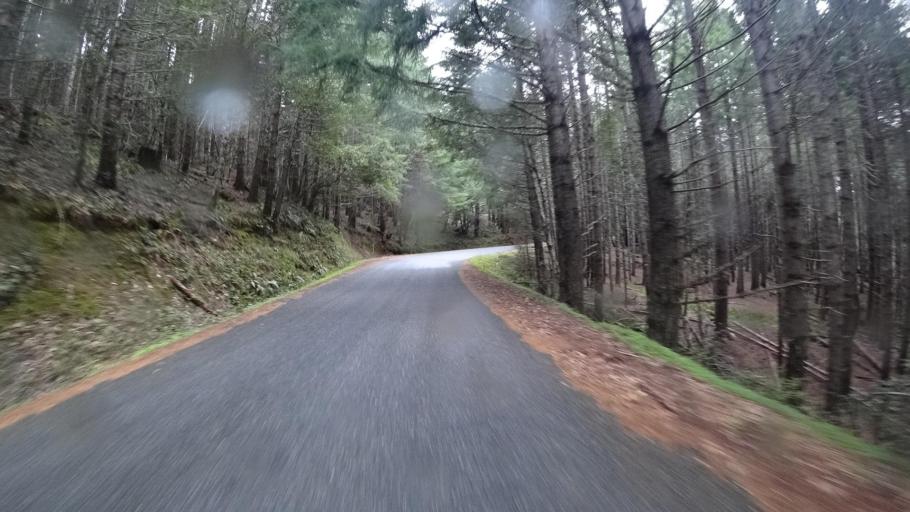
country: US
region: California
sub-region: Humboldt County
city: Willow Creek
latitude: 41.2003
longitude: -123.7784
